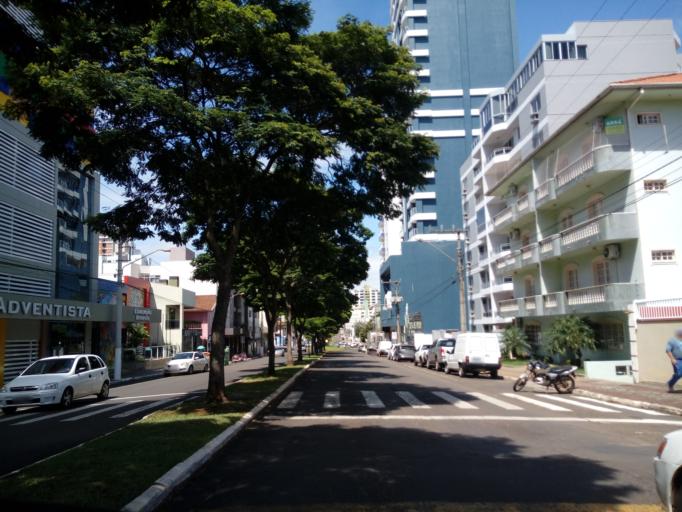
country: BR
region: Santa Catarina
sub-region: Chapeco
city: Chapeco
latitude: -27.1027
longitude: -52.6113
